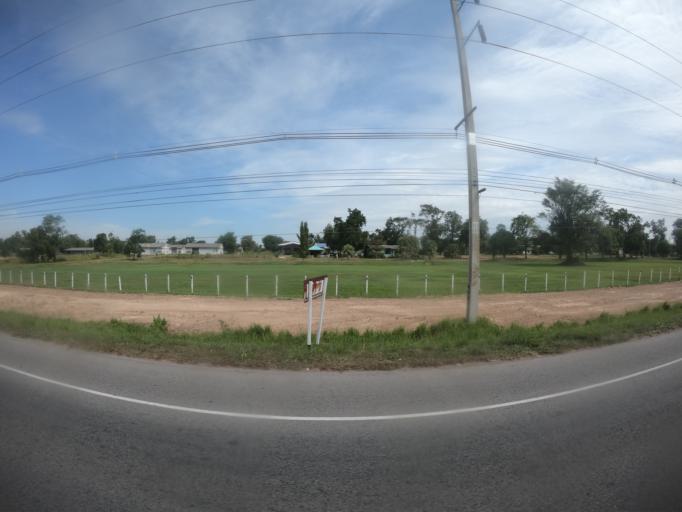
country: TH
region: Maha Sarakham
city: Chiang Yuen
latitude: 16.4320
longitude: 103.0581
